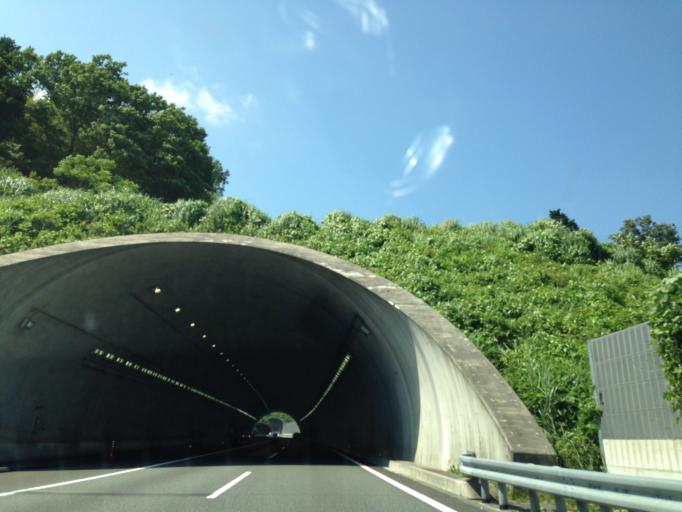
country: JP
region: Shizuoka
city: Mishima
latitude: 35.1946
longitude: 138.8890
